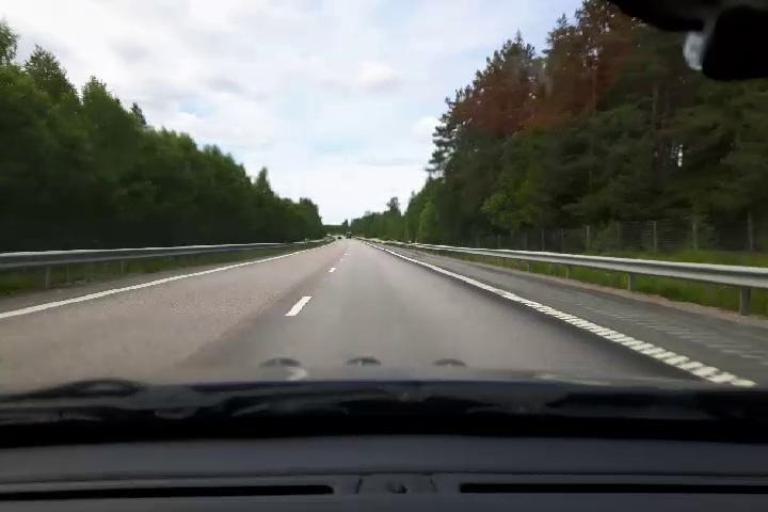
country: SE
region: Uppsala
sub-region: Alvkarleby Kommun
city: AElvkarleby
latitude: 60.4826
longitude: 17.3627
